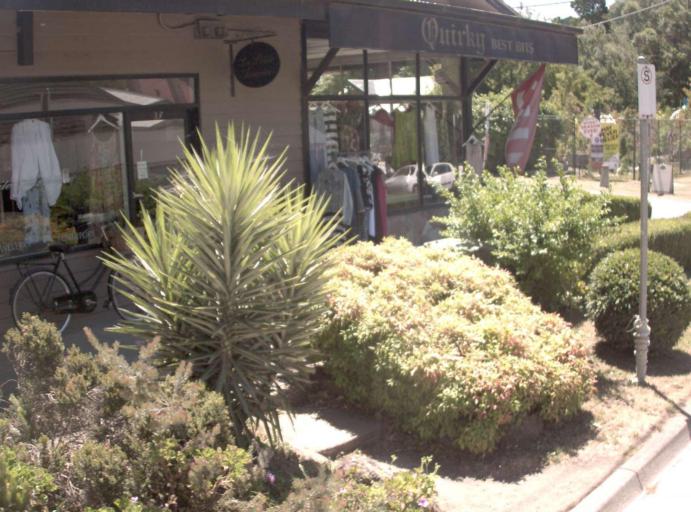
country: AU
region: Victoria
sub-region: Yarra Ranges
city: Olinda
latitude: -37.8638
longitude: 145.3530
